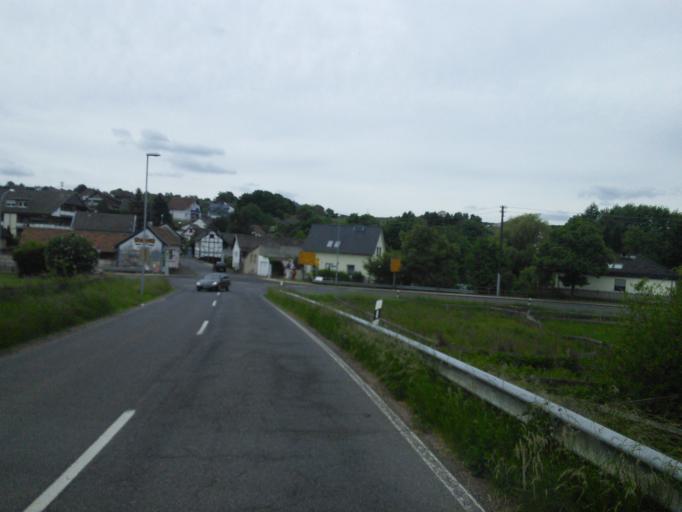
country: DE
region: North Rhine-Westphalia
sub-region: Regierungsbezirk Koln
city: Rheinbach
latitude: 50.5985
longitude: 6.8921
